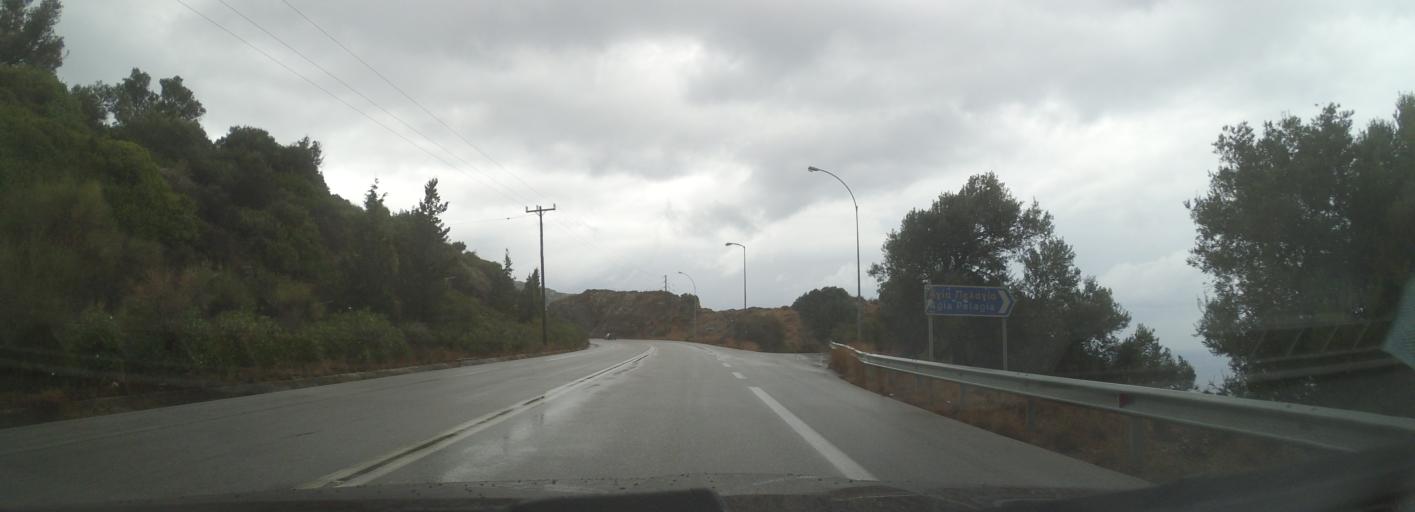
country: GR
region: Crete
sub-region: Nomos Irakleiou
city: Gazi
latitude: 35.4061
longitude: 24.9918
